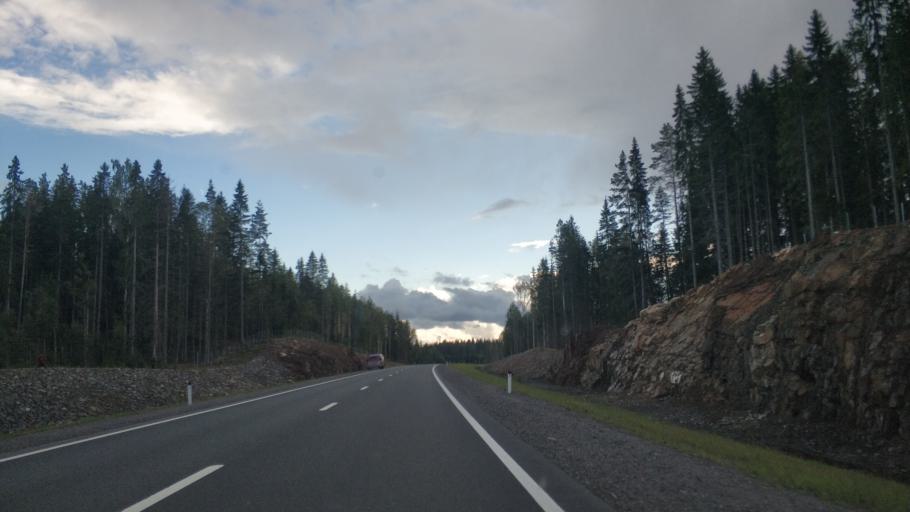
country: RU
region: Republic of Karelia
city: Lakhdenpokh'ya
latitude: 61.4590
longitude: 29.9988
